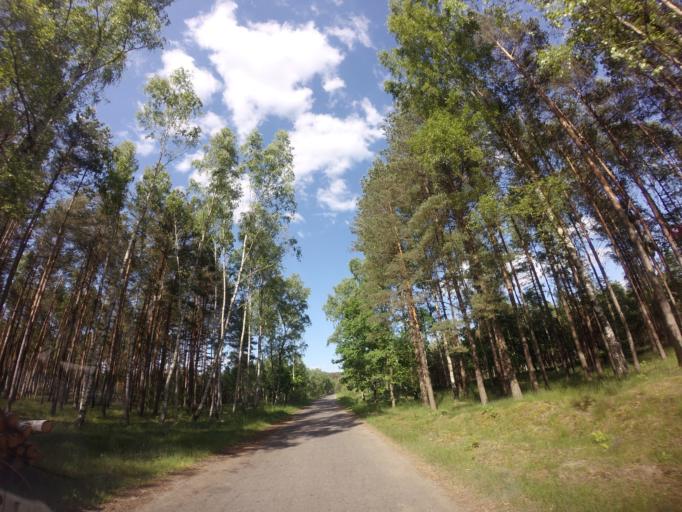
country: PL
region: West Pomeranian Voivodeship
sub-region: Powiat choszczenski
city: Drawno
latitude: 53.1854
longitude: 15.8671
